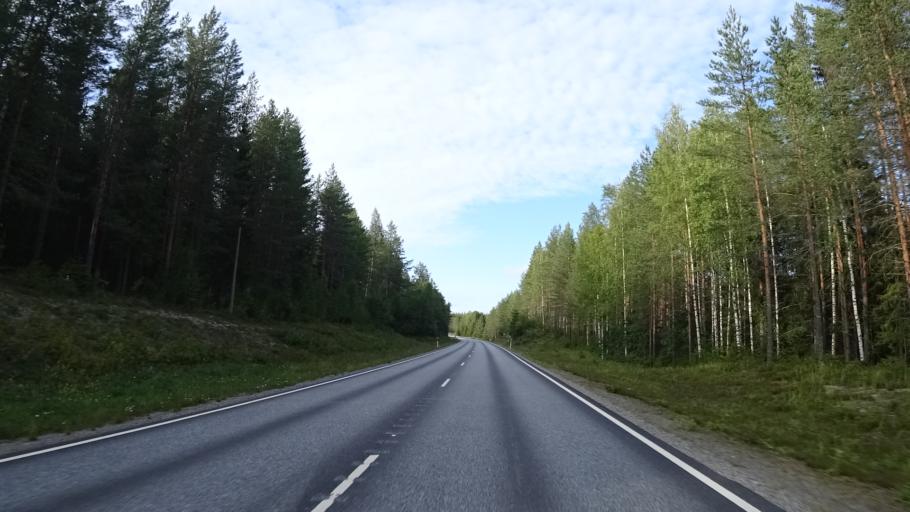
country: FI
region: North Karelia
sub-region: Joensuu
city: Eno
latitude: 62.8234
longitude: 30.1925
